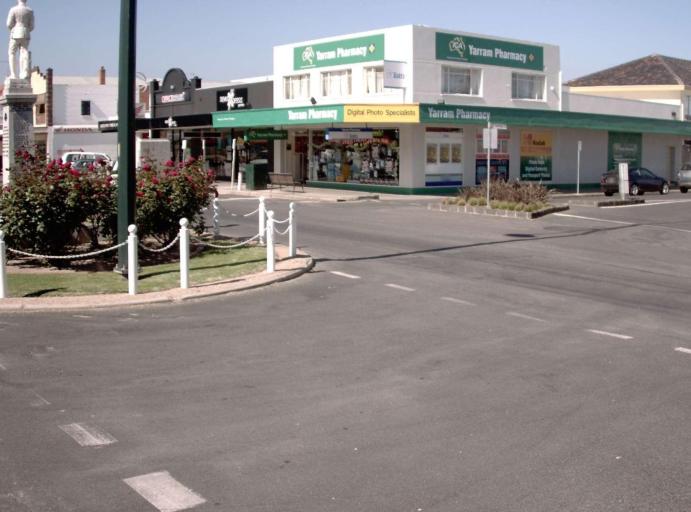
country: AU
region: Victoria
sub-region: Latrobe
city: Traralgon
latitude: -38.5627
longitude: 146.6761
